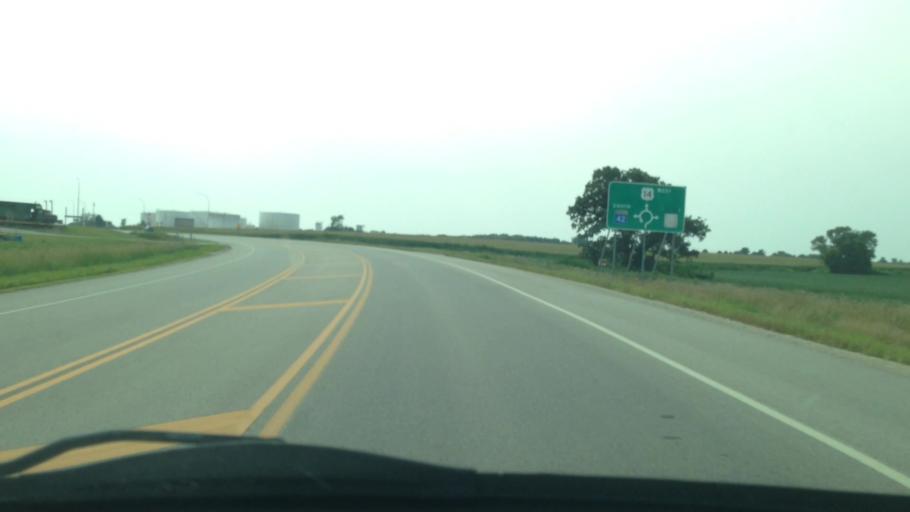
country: US
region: Minnesota
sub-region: Olmsted County
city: Eyota
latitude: 43.9985
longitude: -92.2430
